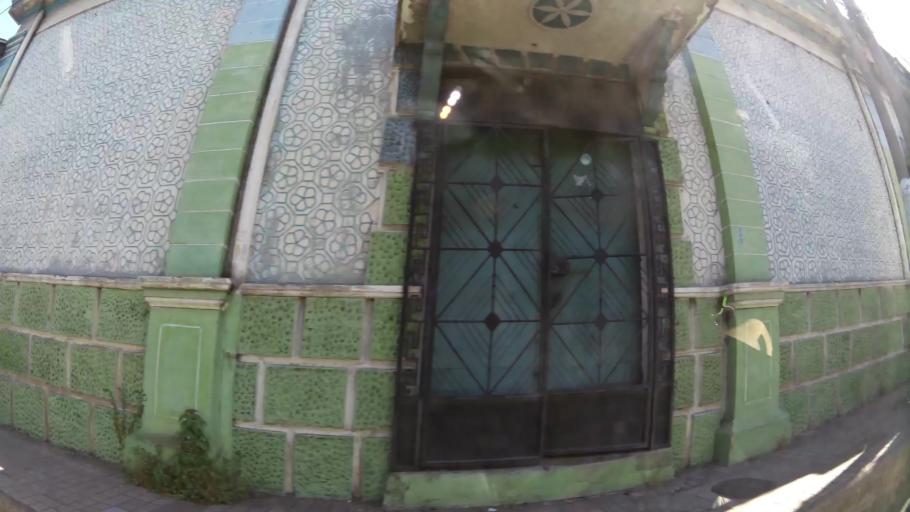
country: SV
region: San Miguel
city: San Miguel
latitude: 13.4874
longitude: -88.1754
